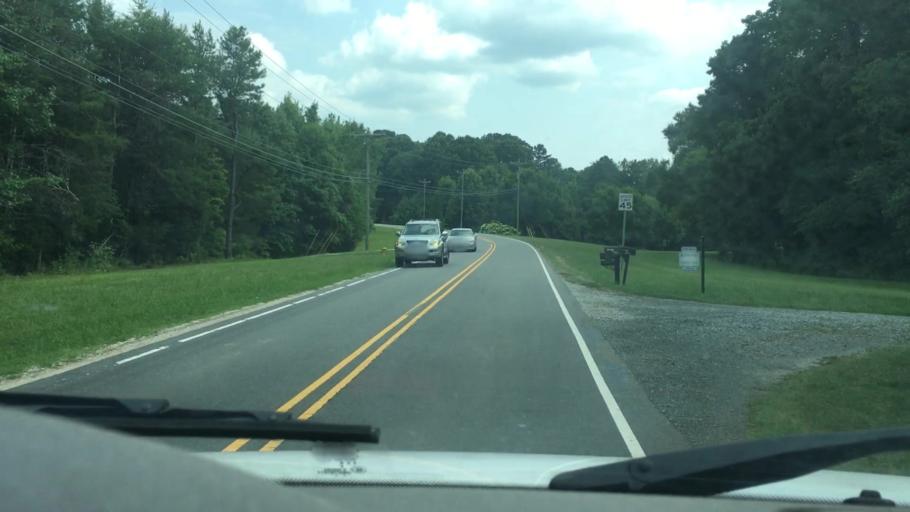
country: US
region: North Carolina
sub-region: Gaston County
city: Davidson
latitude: 35.4710
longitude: -80.8162
